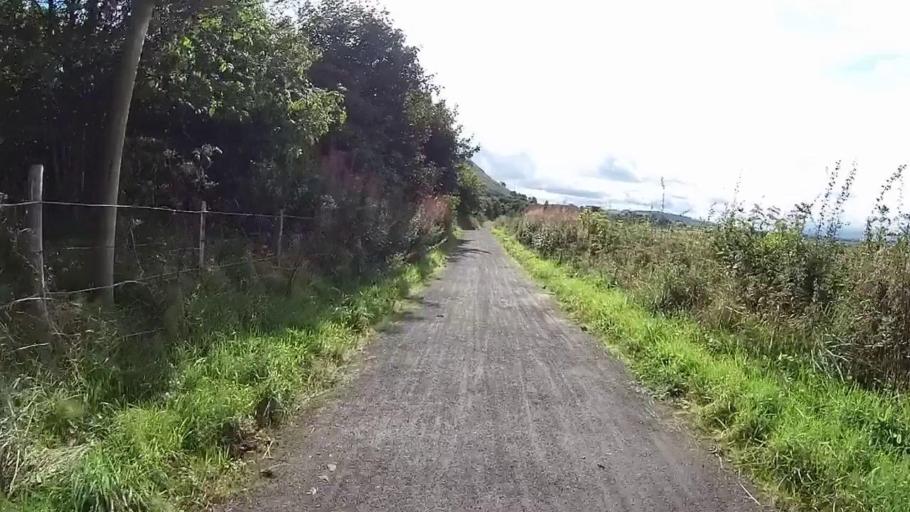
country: GB
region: Scotland
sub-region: Fife
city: Ballingry
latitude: 56.1746
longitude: -3.3594
